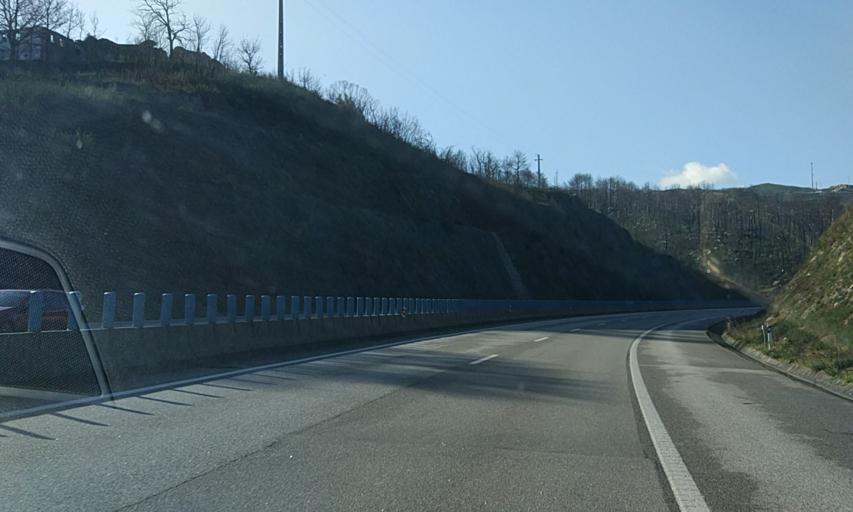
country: PT
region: Viseu
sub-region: Vouzela
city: Vouzela
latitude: 40.6961
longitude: -8.0939
